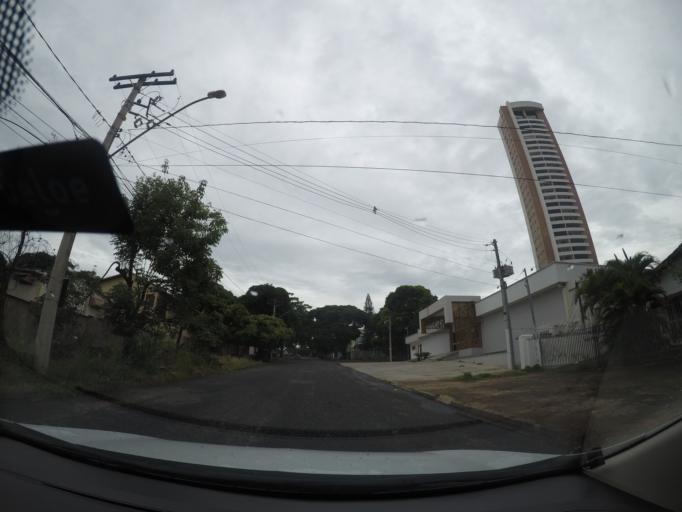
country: BR
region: Goias
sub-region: Goiania
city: Goiania
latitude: -16.6806
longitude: -49.2410
